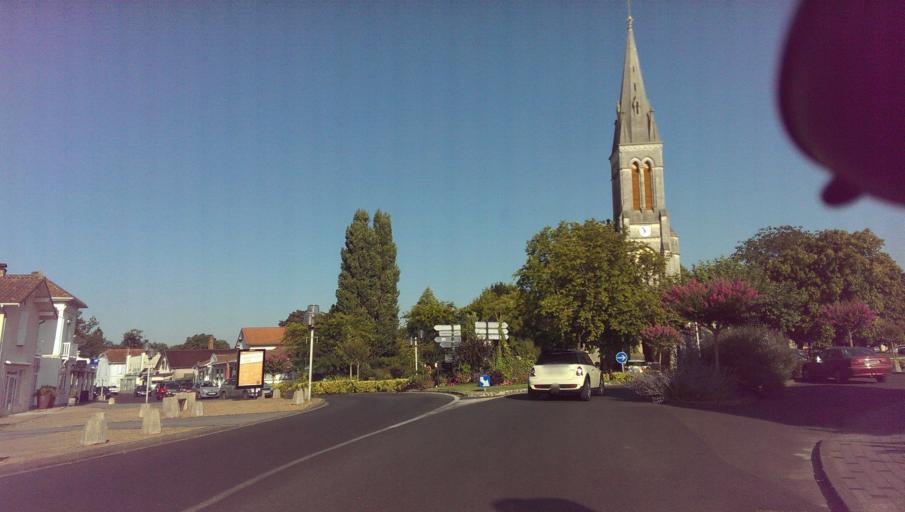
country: FR
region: Aquitaine
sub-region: Departement des Landes
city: Mimizan
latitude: 44.2027
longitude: -1.2299
